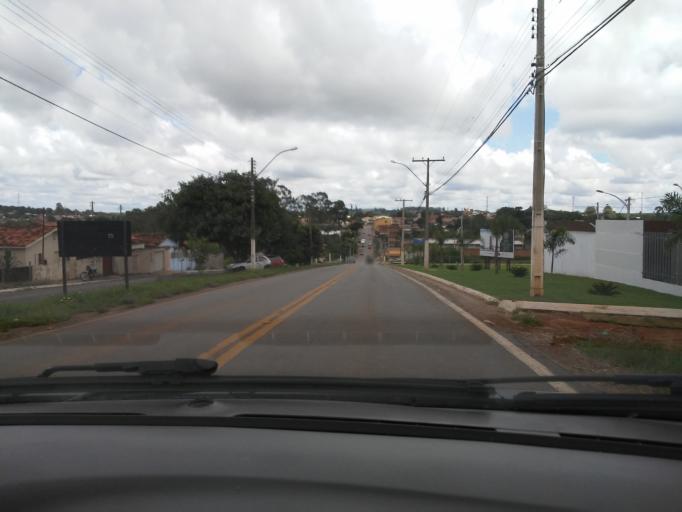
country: BR
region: Goias
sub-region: Ipameri
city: Ipameri
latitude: -17.7346
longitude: -48.1619
